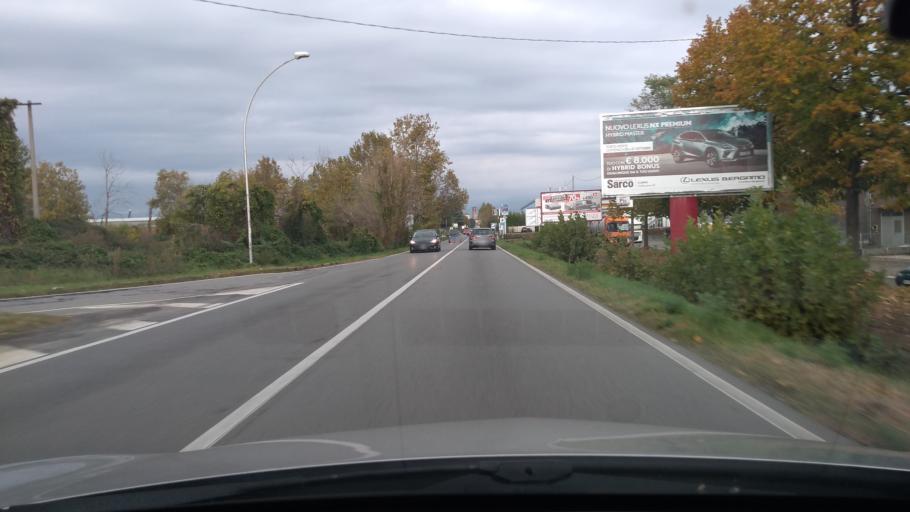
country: IT
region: Lombardy
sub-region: Provincia di Bergamo
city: Verdello
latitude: 45.5937
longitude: 9.6217
